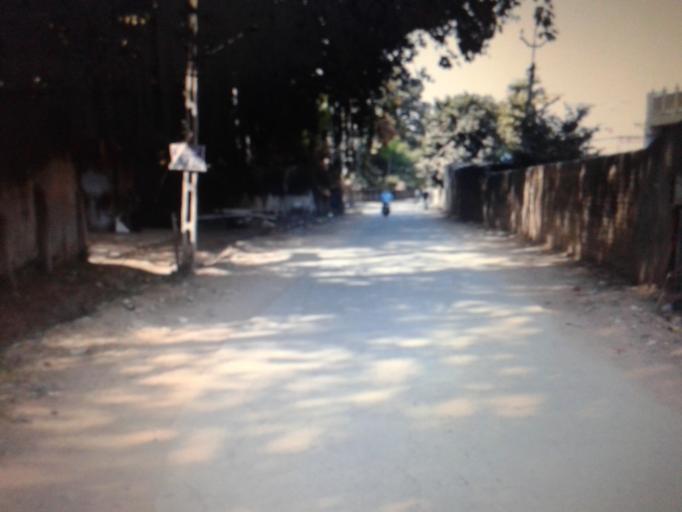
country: IN
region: Gujarat
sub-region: Anand
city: Karamsad
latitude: 22.5488
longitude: 72.9227
